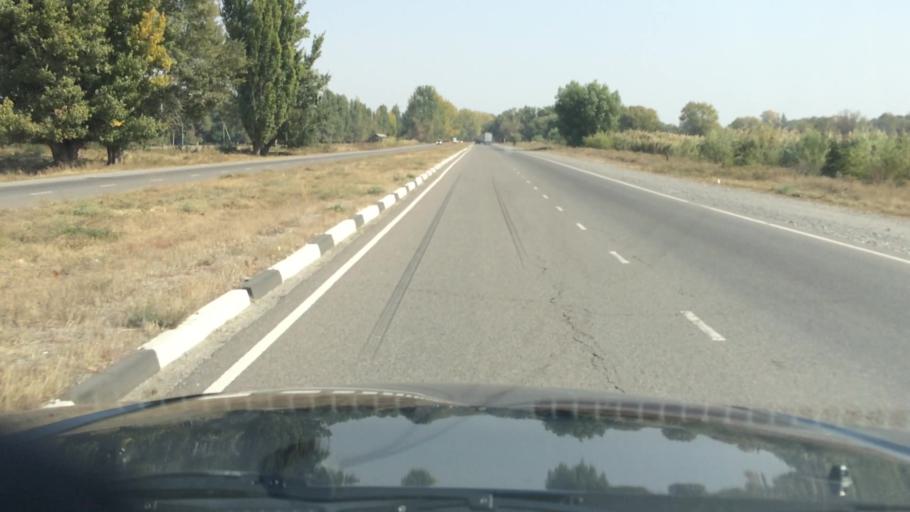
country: KG
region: Chuy
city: Kant
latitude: 42.9706
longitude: 74.8512
